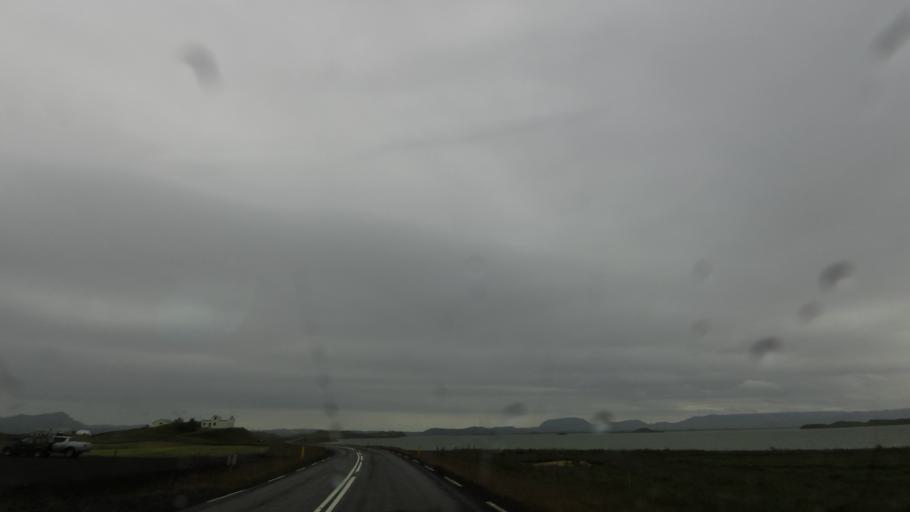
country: IS
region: Northeast
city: Laugar
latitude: 65.6127
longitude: -17.0825
